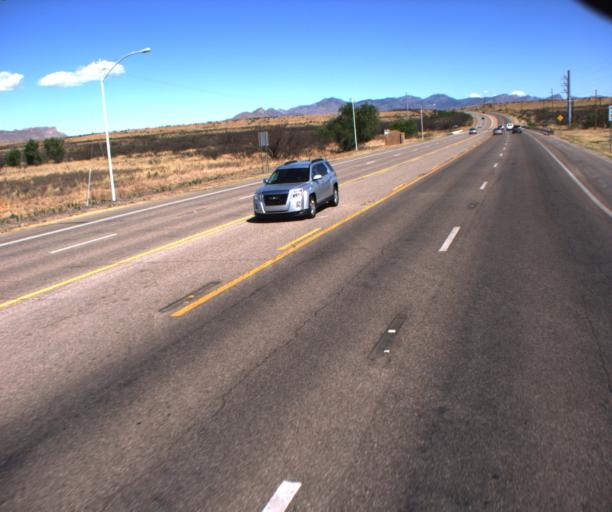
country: US
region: Arizona
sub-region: Cochise County
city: Huachuca City
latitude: 31.6433
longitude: -110.3396
